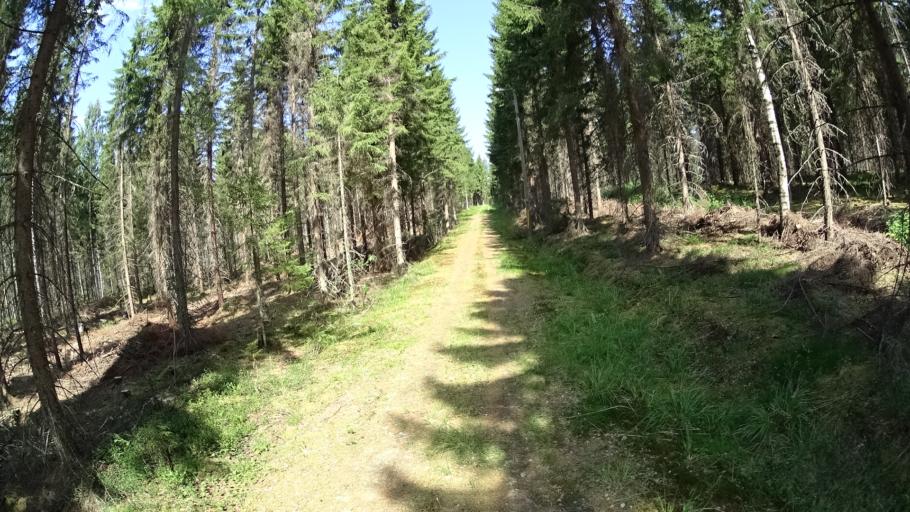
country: FI
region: North Karelia
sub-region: Pielisen Karjala
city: Lieksa
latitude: 63.1263
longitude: 29.7993
